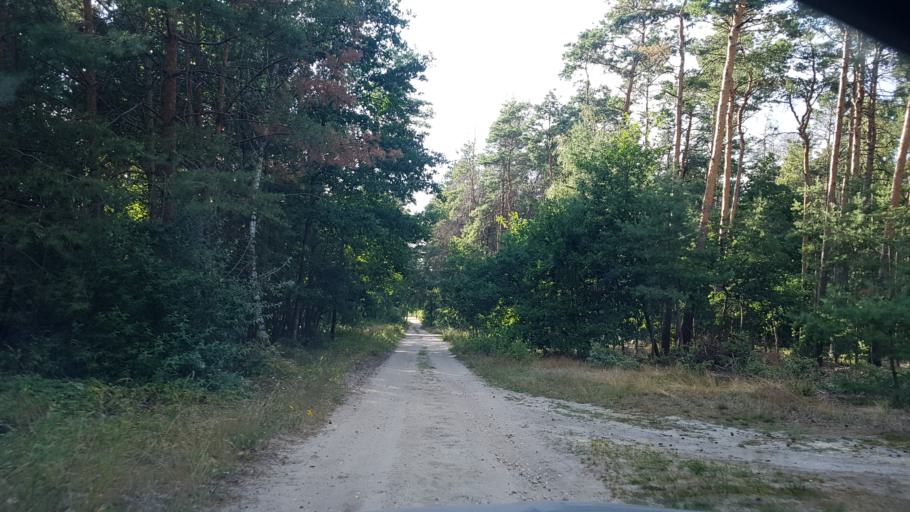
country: DE
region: Brandenburg
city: Schilda
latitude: 51.6417
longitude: 13.3918
